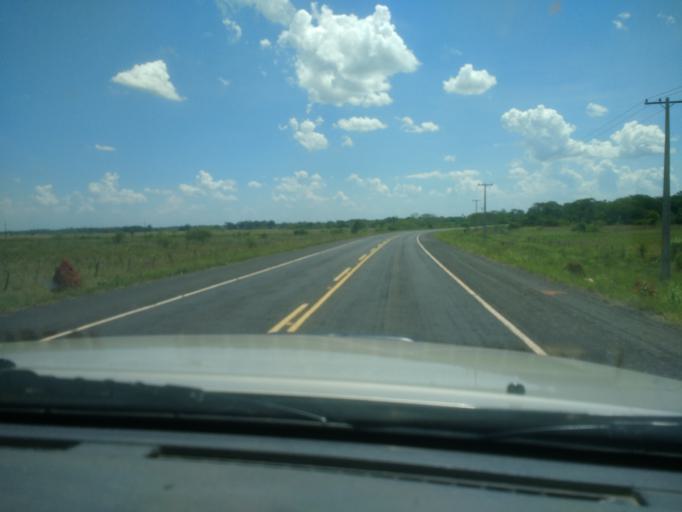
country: PY
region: San Pedro
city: Itacurubi del Rosario
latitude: -24.5260
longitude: -56.8344
